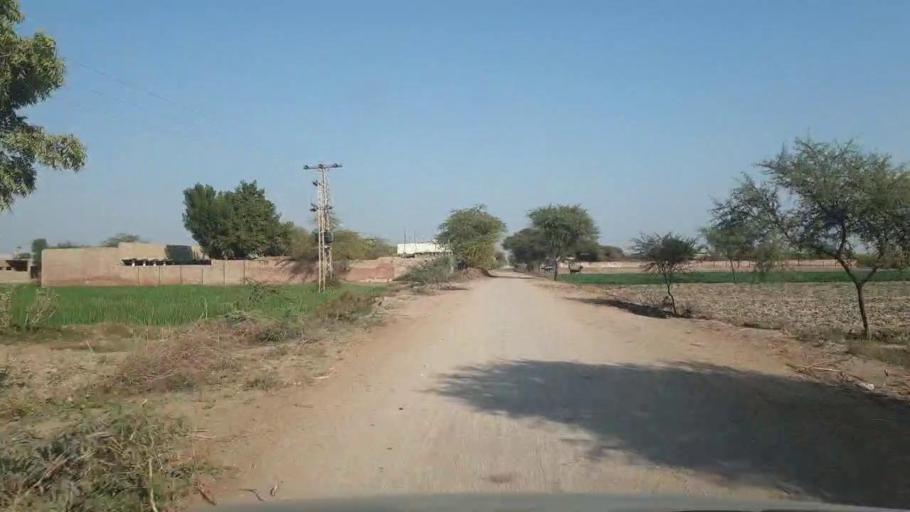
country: PK
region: Sindh
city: Chambar
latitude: 25.2882
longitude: 68.8614
